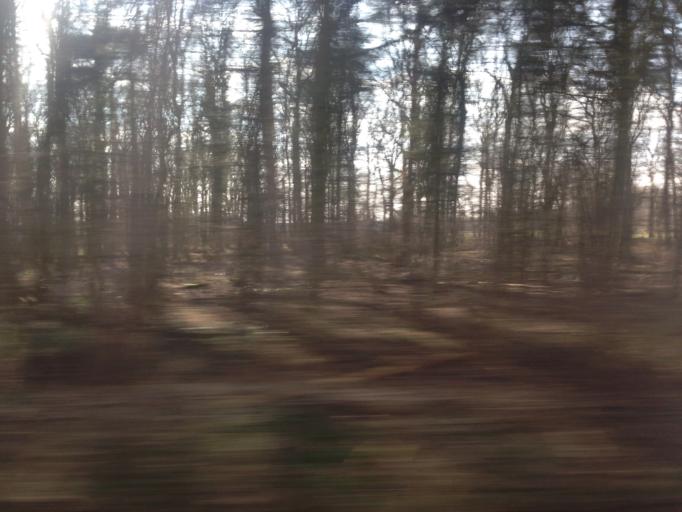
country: DE
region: North Rhine-Westphalia
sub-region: Regierungsbezirk Munster
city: Muenster
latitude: 51.9933
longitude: 7.6342
